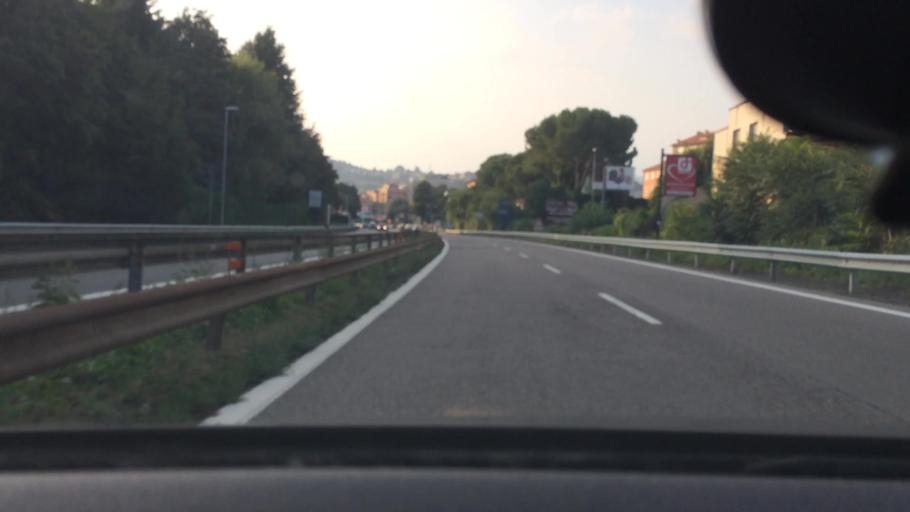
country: IT
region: Lombardy
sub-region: Provincia di Bergamo
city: Bergamo
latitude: 45.6838
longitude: 9.6700
